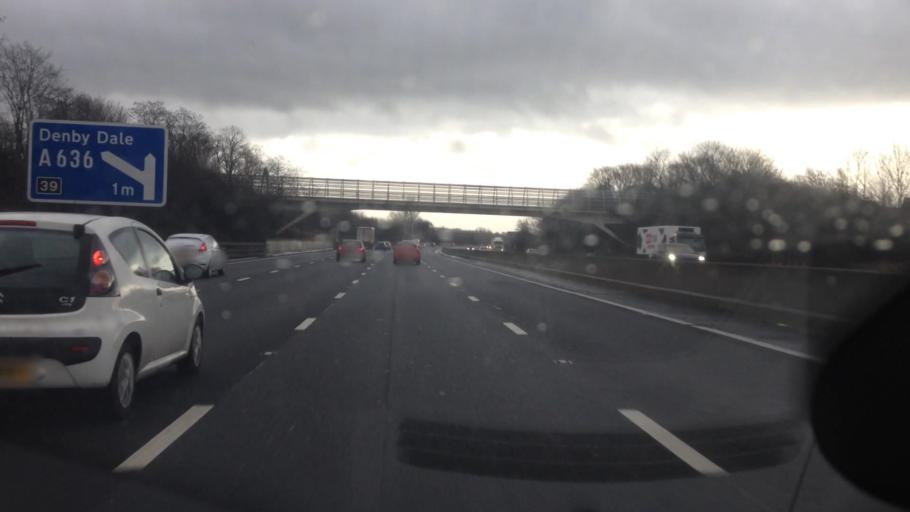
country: GB
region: England
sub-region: City and Borough of Wakefield
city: Horbury
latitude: 53.6688
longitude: -1.5439
